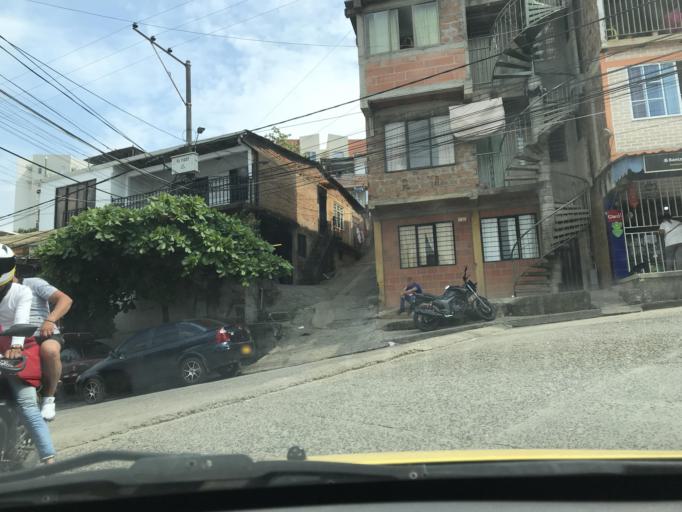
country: CO
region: Valle del Cauca
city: Cali
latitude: 3.3732
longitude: -76.5545
